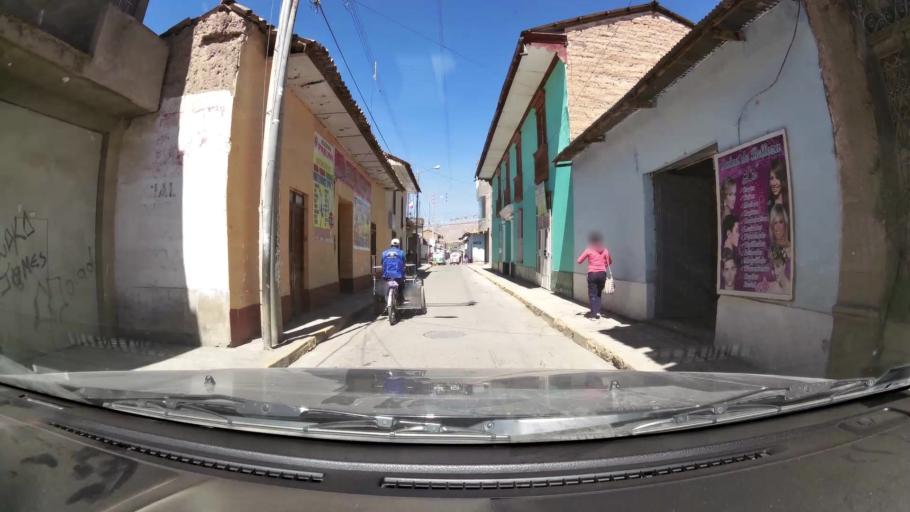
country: PE
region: Junin
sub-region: Provincia de Jauja
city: Jauja
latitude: -11.7755
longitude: -75.4986
